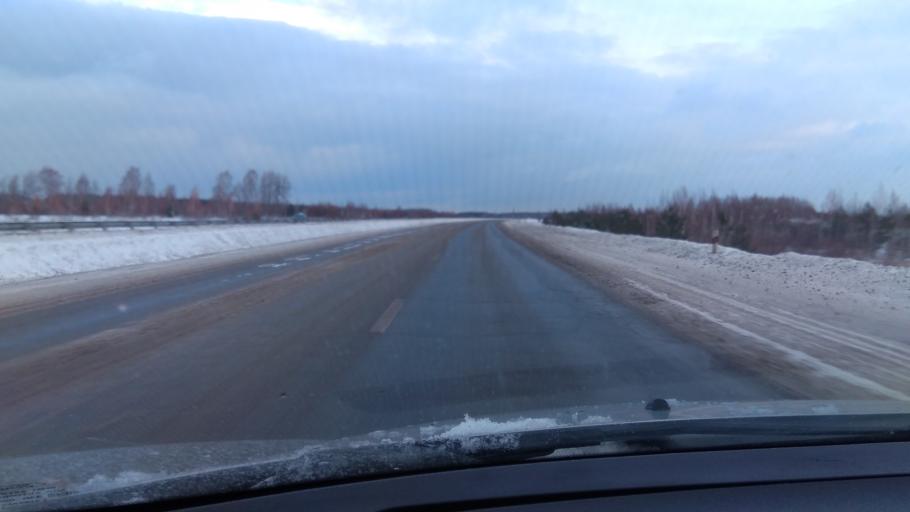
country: RU
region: Sverdlovsk
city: Nev'yansk
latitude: 57.5164
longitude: 60.1795
